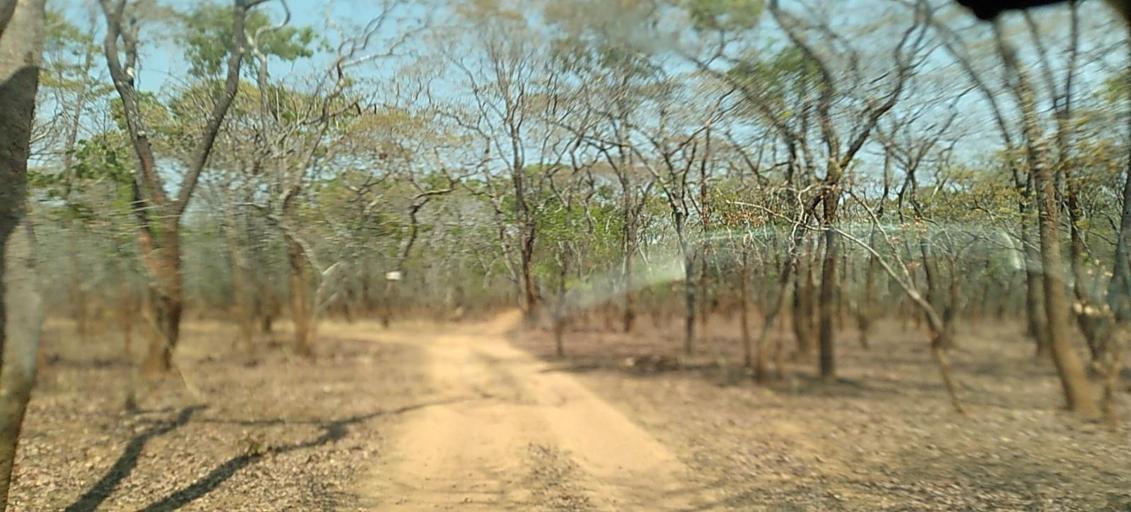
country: ZM
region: North-Western
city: Kasempa
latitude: -13.3934
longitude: 25.5981
